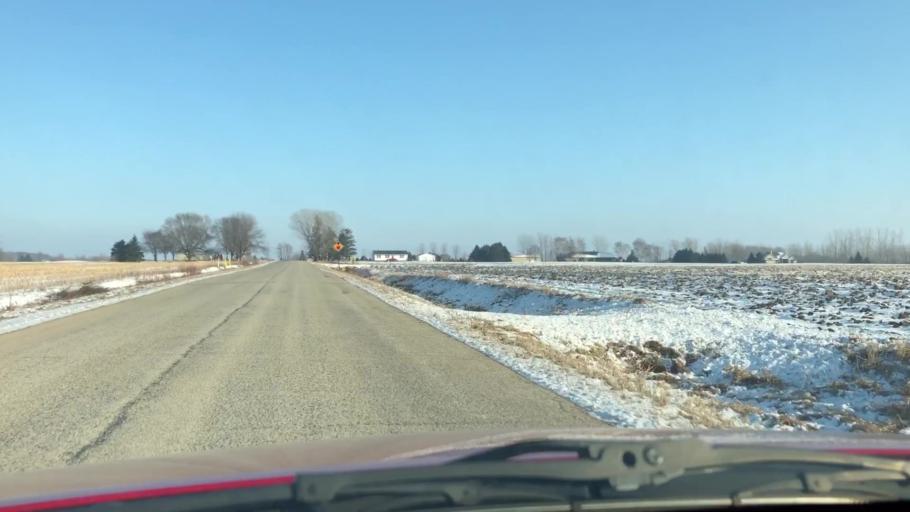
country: US
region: Wisconsin
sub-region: Outagamie County
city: Seymour
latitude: 44.4869
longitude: -88.3134
